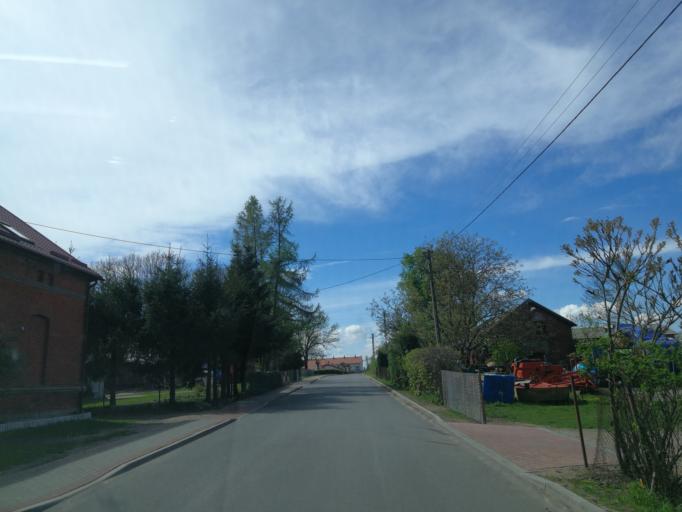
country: PL
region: Warmian-Masurian Voivodeship
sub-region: Powiat ilawski
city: Lubawa
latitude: 53.5980
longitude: 19.7028
